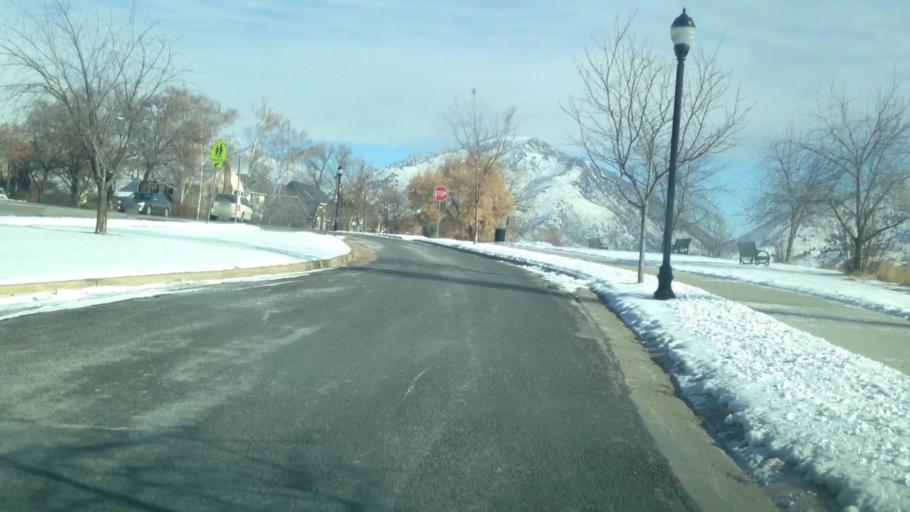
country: US
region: Utah
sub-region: Cache County
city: Logan
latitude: 41.7329
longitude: -111.8277
